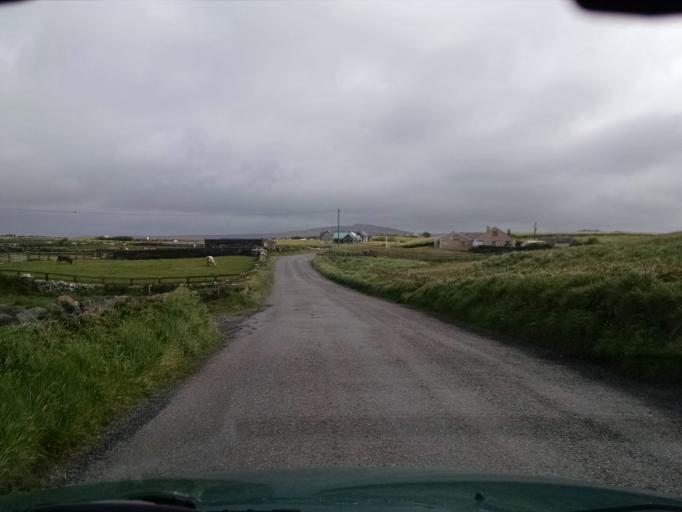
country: IE
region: Connaught
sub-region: County Galway
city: Bearna
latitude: 53.0327
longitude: -9.3643
